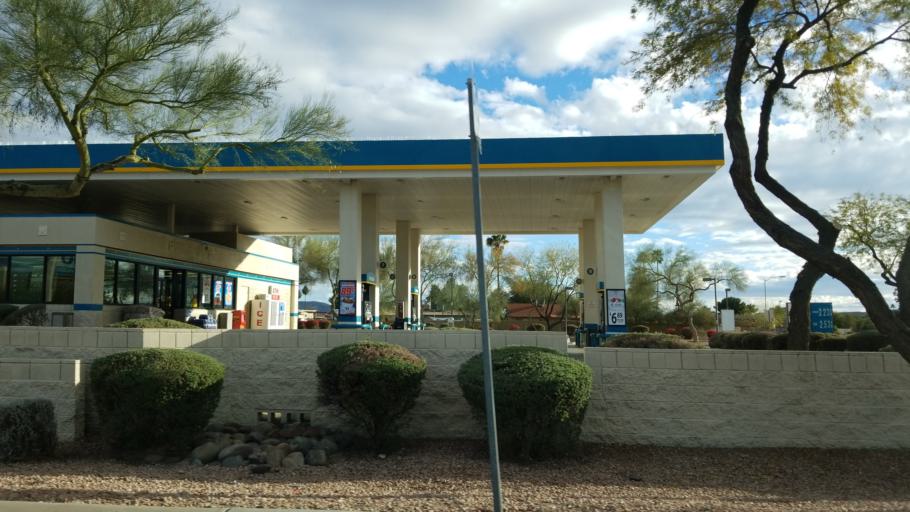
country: US
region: Arizona
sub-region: Maricopa County
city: Glendale
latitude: 33.6546
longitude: -112.1101
